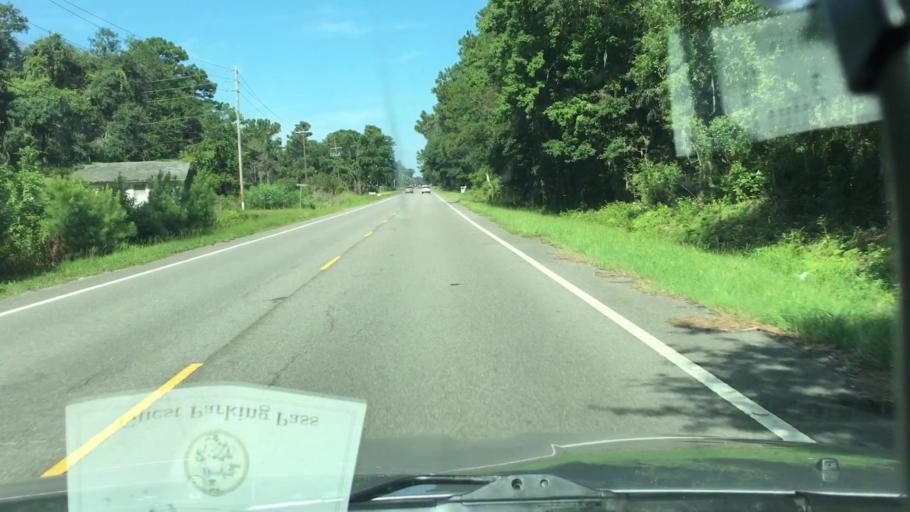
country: US
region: South Carolina
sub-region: Beaufort County
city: Beaufort
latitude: 32.4142
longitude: -80.4979
